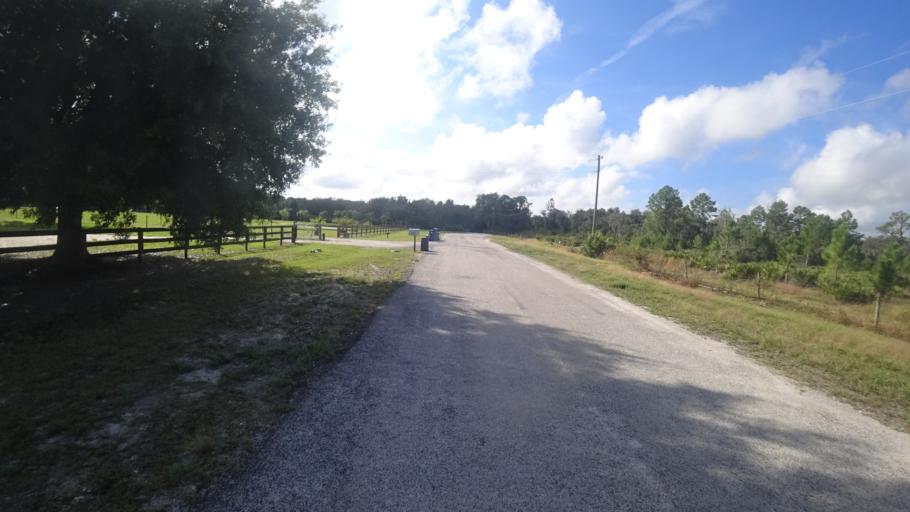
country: US
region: Florida
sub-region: Hillsborough County
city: Wimauma
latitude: 27.4421
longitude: -82.1365
